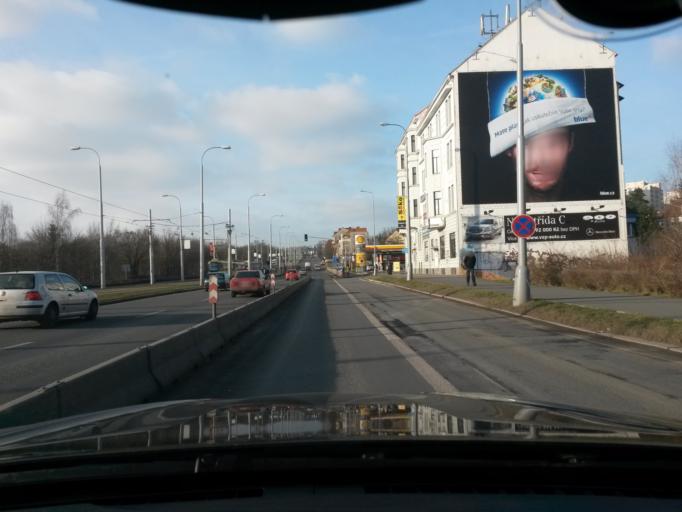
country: CZ
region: Plzensky
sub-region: Okres Plzen-Mesto
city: Pilsen
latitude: 49.7568
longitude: 13.3738
